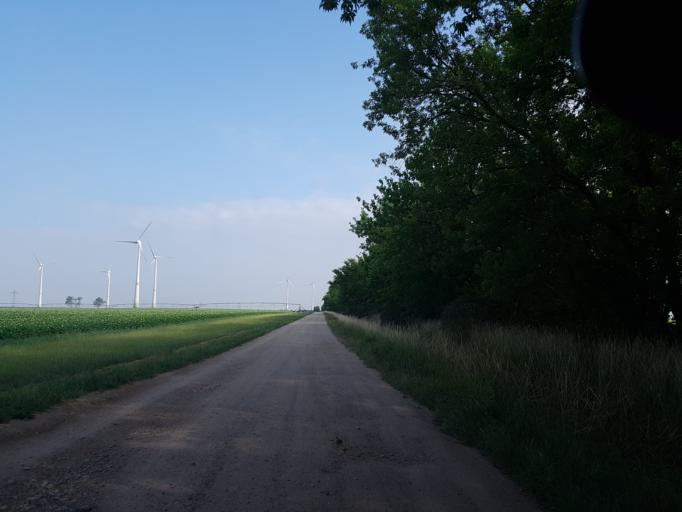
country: DE
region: Saxony-Anhalt
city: Zahna
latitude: 51.9840
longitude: 12.8222
